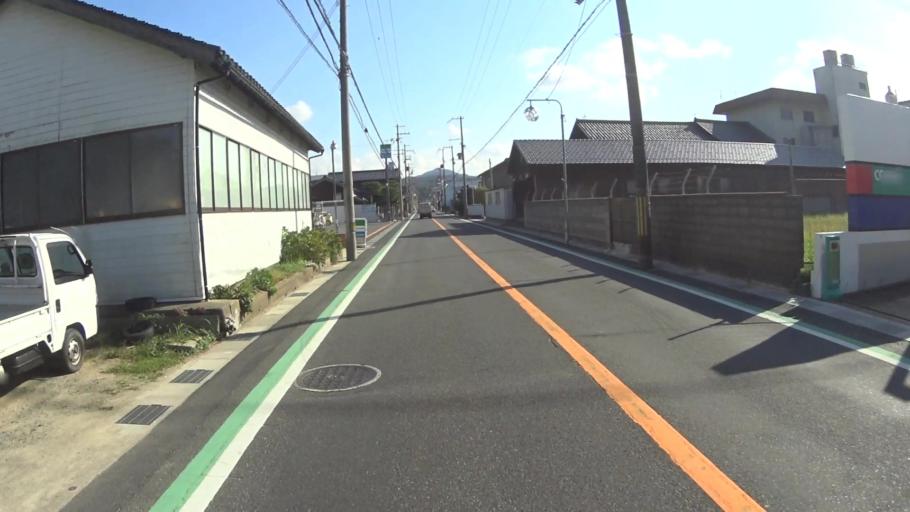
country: JP
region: Kyoto
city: Miyazu
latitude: 35.6768
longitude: 135.0283
